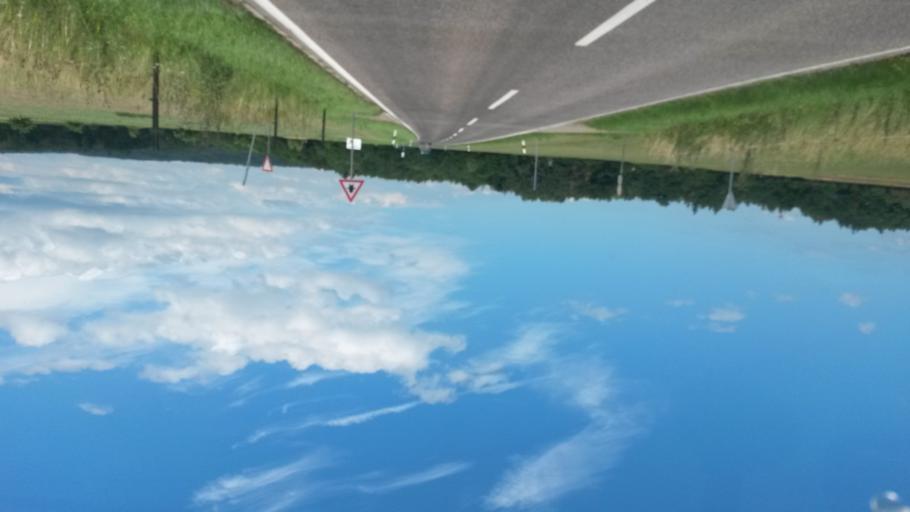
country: DE
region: Baden-Wuerttemberg
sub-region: Karlsruhe Region
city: Unterreichenbach
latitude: 48.8572
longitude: 8.7056
